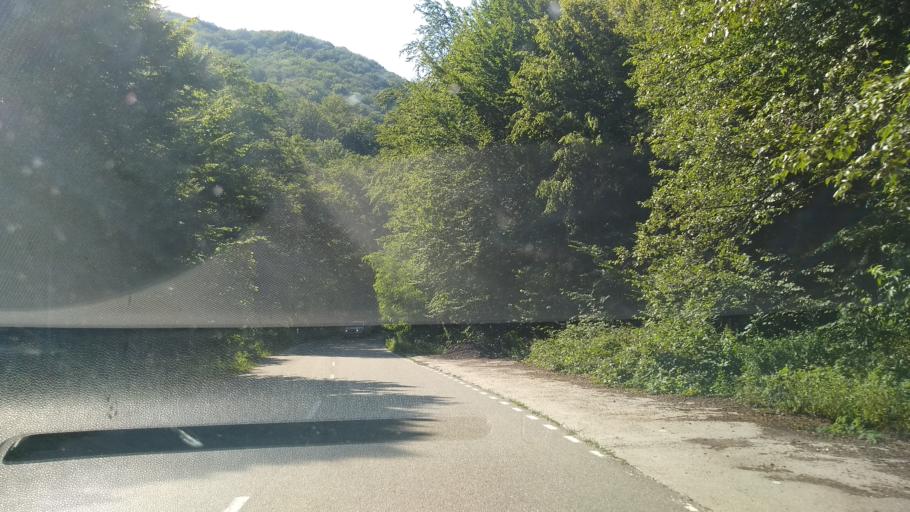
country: RO
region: Hunedoara
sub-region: Comuna Orastioara de Sus
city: Orastioara de Sus
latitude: 45.6435
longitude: 23.1966
